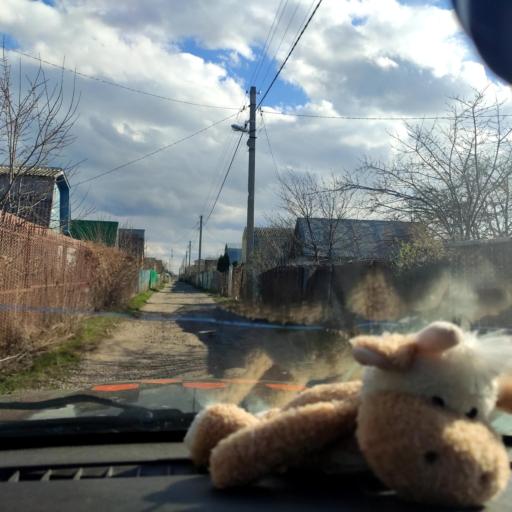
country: RU
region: Samara
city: Tol'yatti
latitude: 53.5941
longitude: 49.3086
